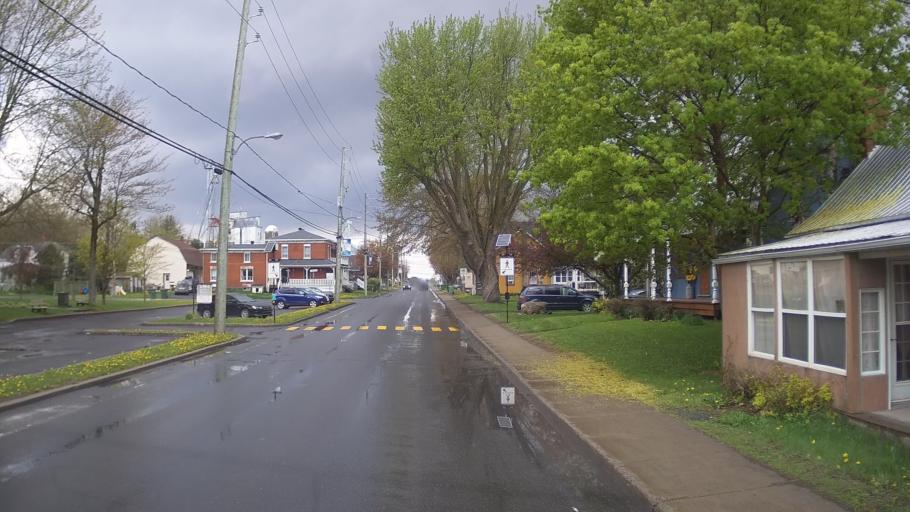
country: CA
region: Quebec
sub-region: Monteregie
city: Farnham
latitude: 45.3226
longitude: -73.0642
